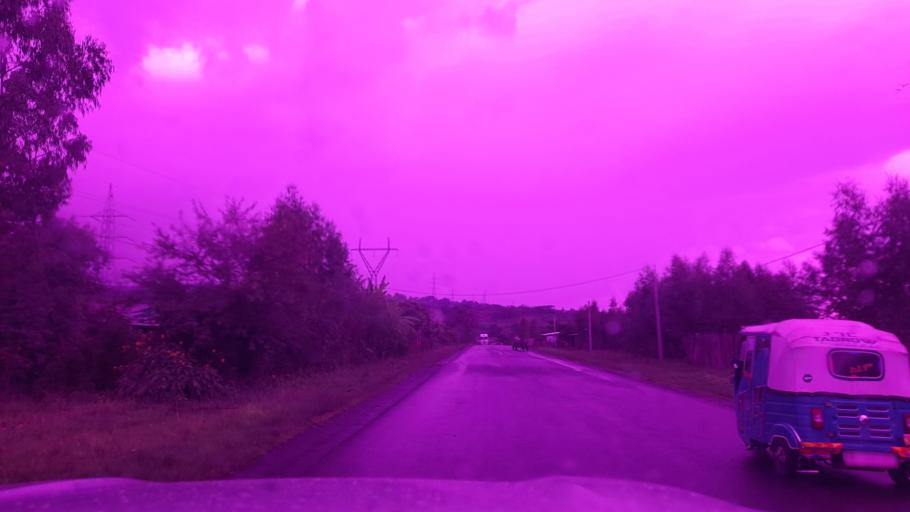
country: ET
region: Oromiya
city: Jima
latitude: 7.7121
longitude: 37.0823
